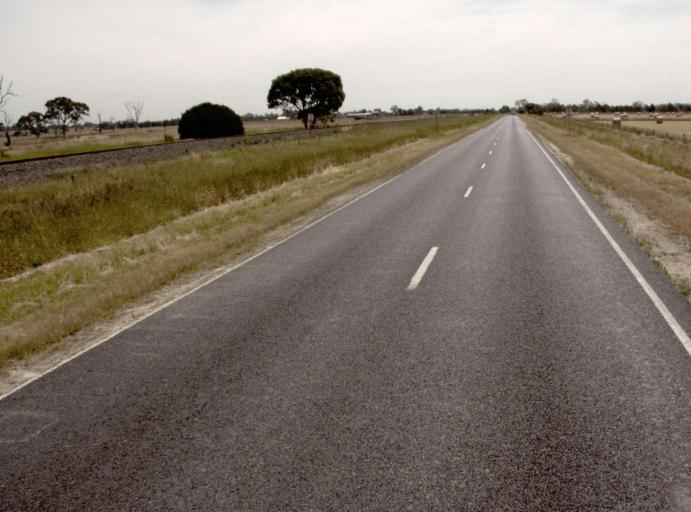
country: AU
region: Victoria
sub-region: Wellington
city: Heyfield
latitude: -38.1549
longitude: 146.8279
